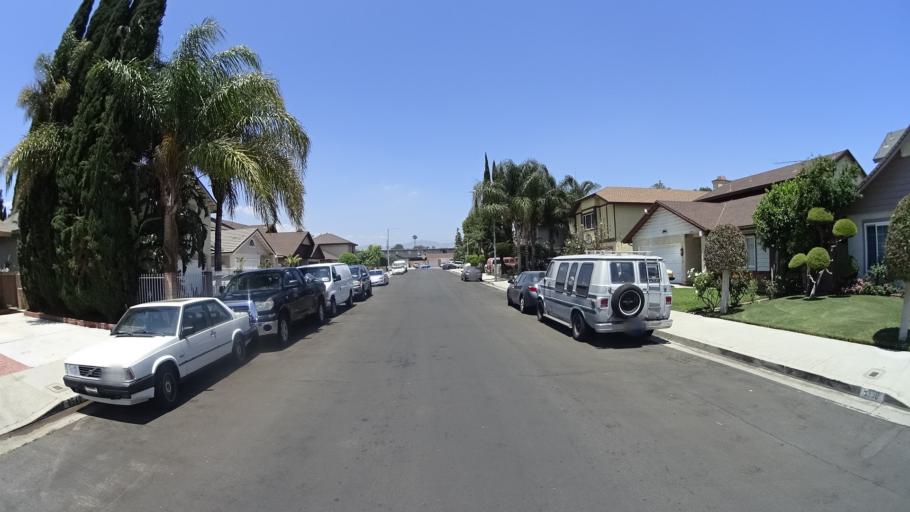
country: US
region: California
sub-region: Los Angeles County
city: Van Nuys
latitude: 34.2261
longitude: -118.4602
